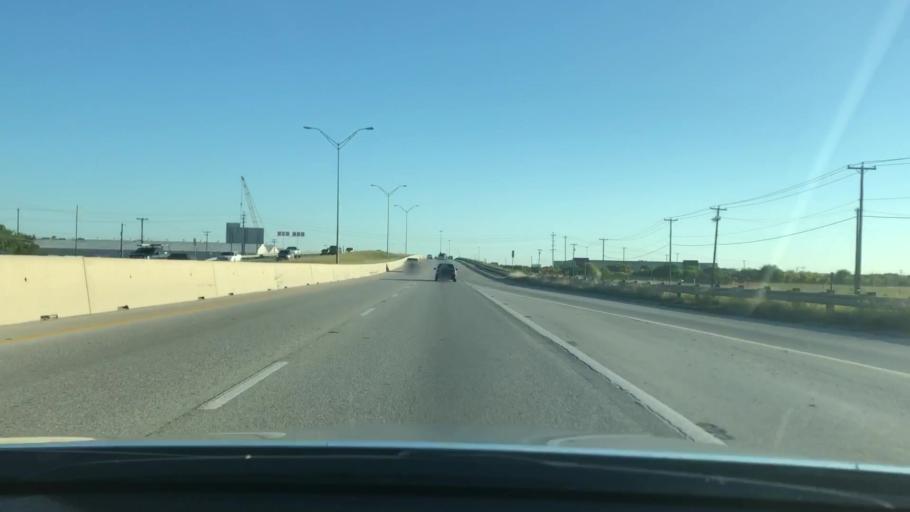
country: US
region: Texas
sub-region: Bexar County
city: Kirby
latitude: 29.4630
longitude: -98.4043
